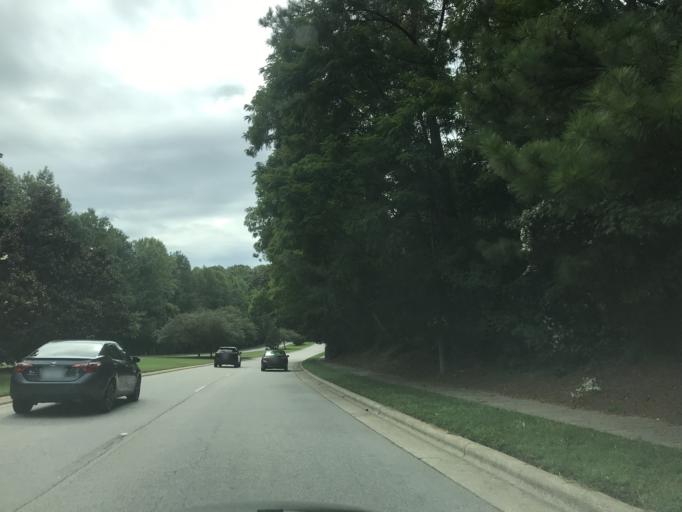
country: US
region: North Carolina
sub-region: Wake County
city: Cary
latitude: 35.7552
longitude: -78.8012
